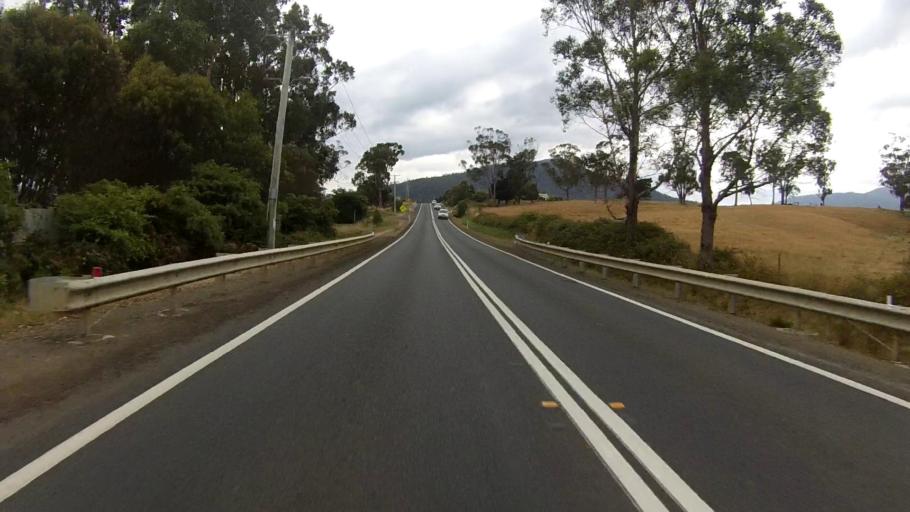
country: AU
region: Tasmania
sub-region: Huon Valley
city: Franklin
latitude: -43.0758
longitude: 147.0340
